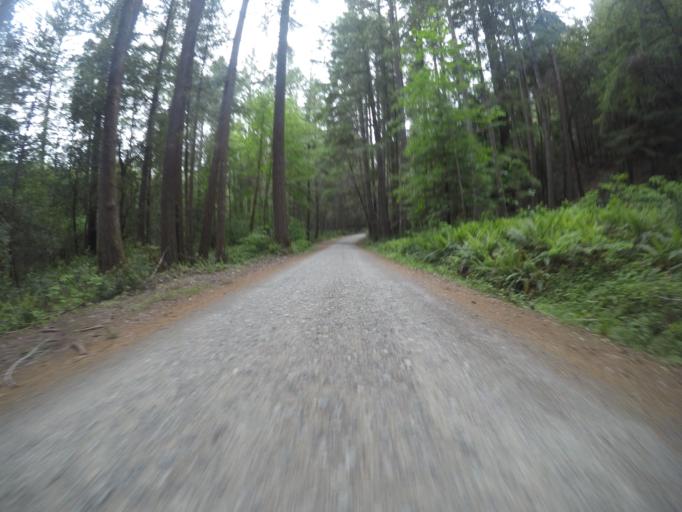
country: US
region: California
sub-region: Del Norte County
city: Bertsch-Oceanview
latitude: 41.7023
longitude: -123.8986
